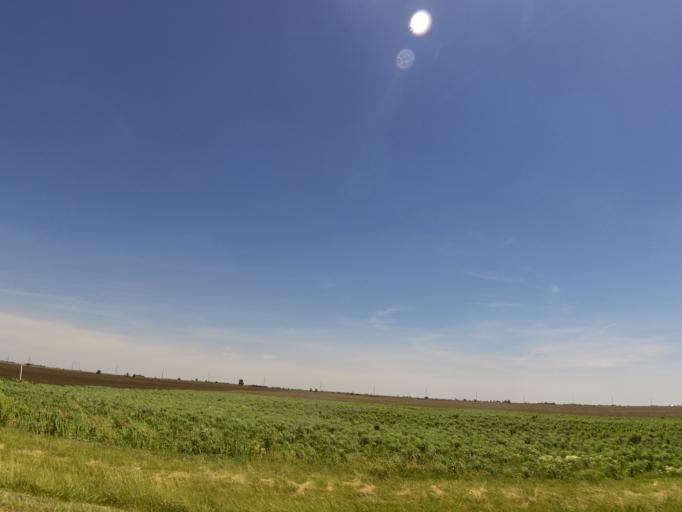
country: US
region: Illinois
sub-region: Iroquois County
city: Milford
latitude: 40.5546
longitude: -87.6931
